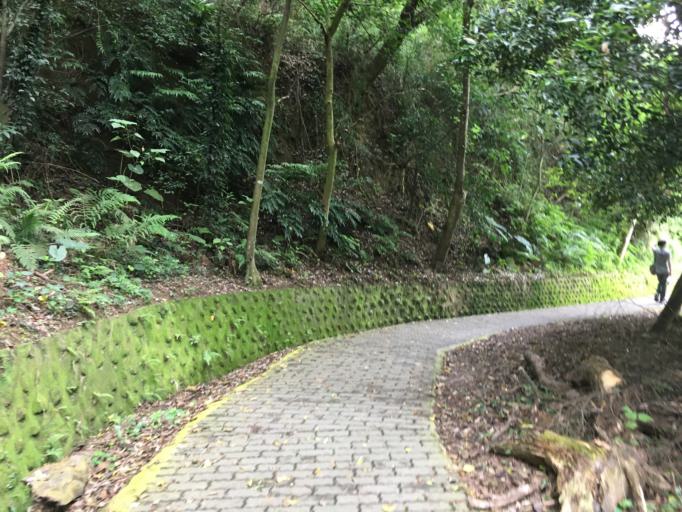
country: TW
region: Taiwan
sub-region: Hsinchu
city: Hsinchu
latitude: 24.7521
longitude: 121.0464
